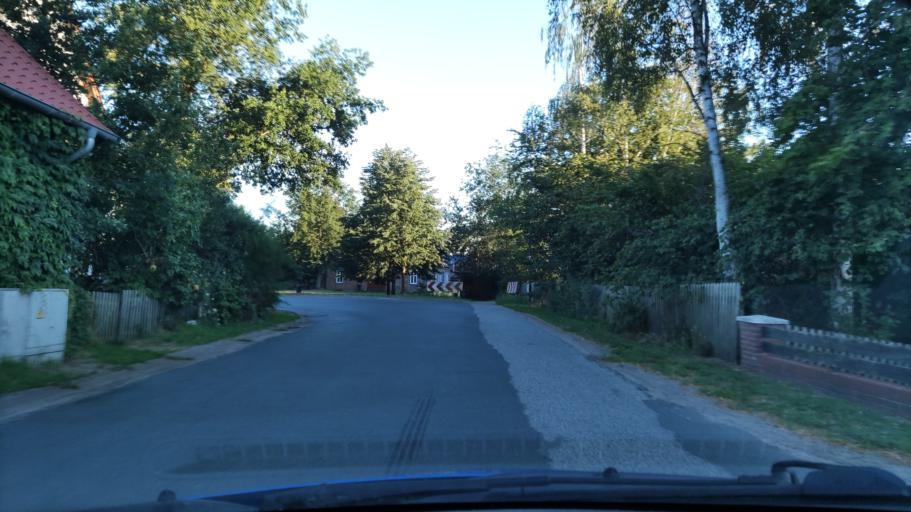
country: DE
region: Lower Saxony
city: Jameln
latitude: 53.0272
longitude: 11.1265
